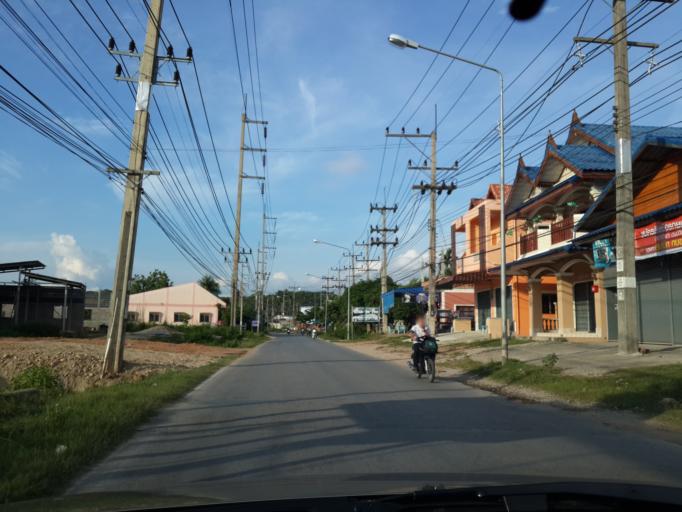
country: TH
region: Yala
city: Yala
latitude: 6.5096
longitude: 101.2704
